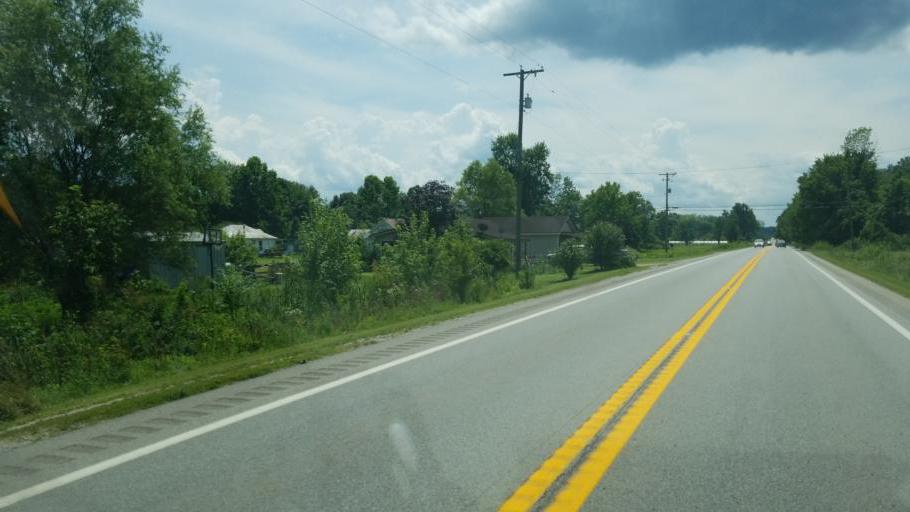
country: US
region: West Virginia
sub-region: Putnam County
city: Buffalo
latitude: 38.6214
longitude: -81.9869
